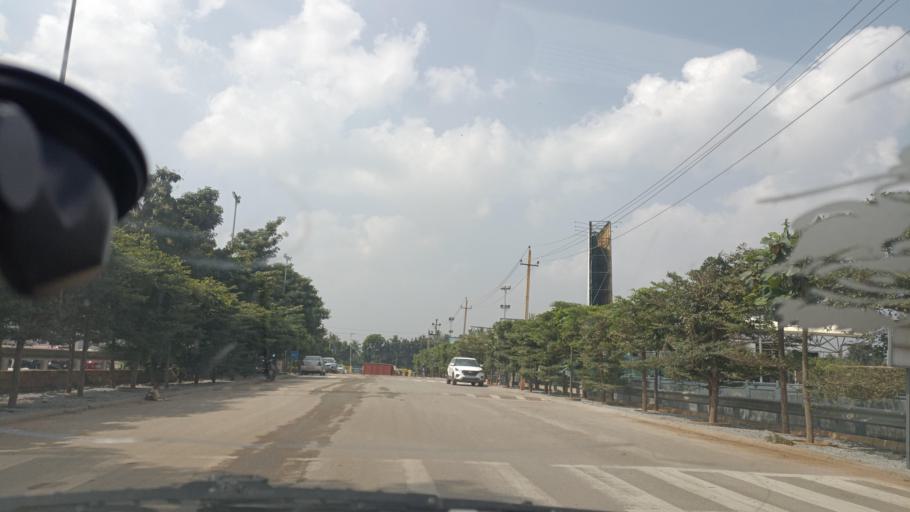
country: IN
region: Karnataka
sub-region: Bangalore Urban
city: Yelahanka
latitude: 13.1691
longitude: 77.6332
